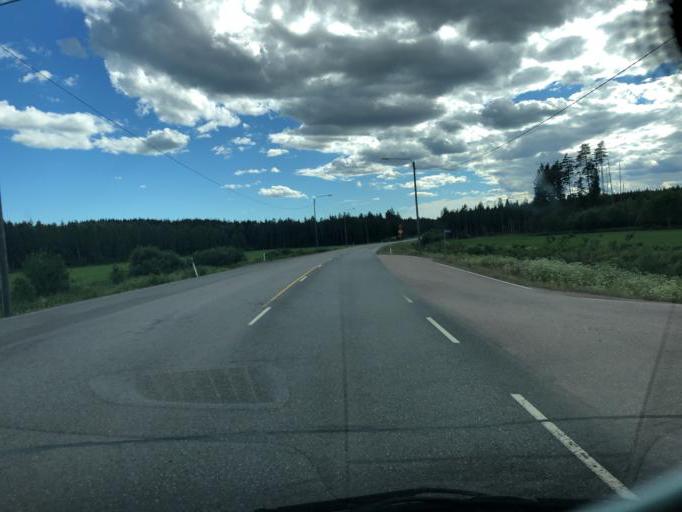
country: FI
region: Kymenlaakso
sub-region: Kouvola
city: Kouvola
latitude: 61.0288
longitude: 26.9839
